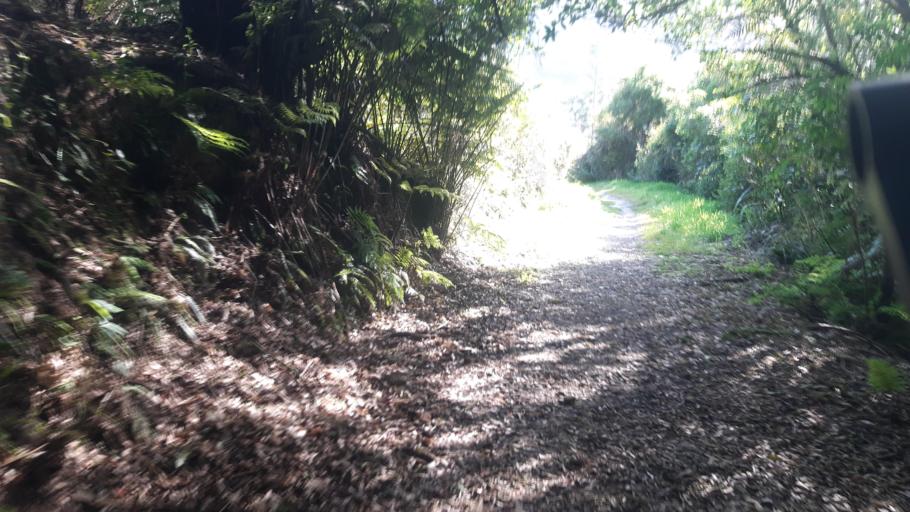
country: NZ
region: Marlborough
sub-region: Marlborough District
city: Picton
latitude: -41.2839
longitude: 173.7796
